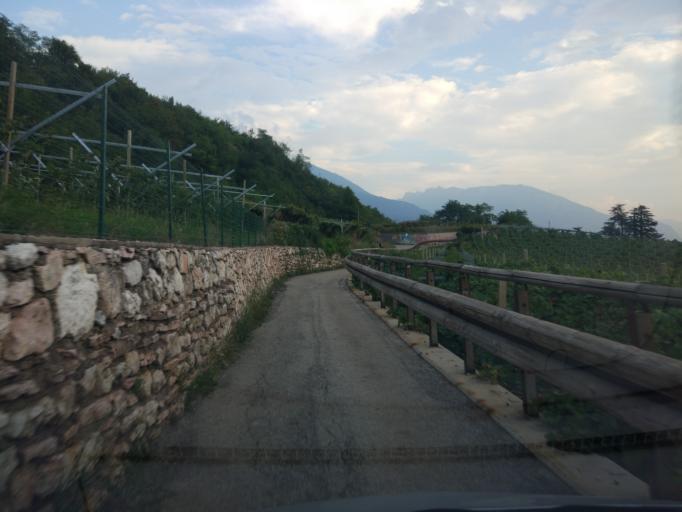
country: IT
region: Trentino-Alto Adige
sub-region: Provincia di Trento
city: Trento
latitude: 46.0858
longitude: 11.1377
